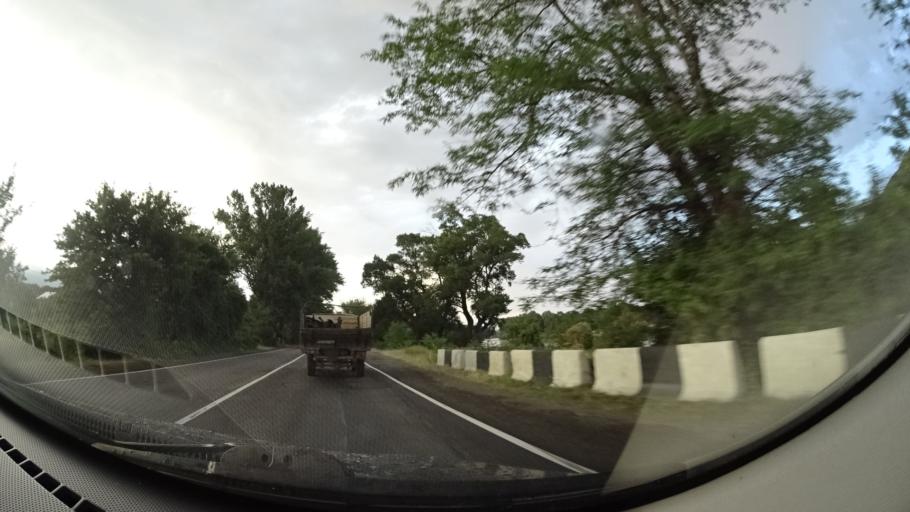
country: GE
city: Surami
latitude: 41.9592
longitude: 43.5098
